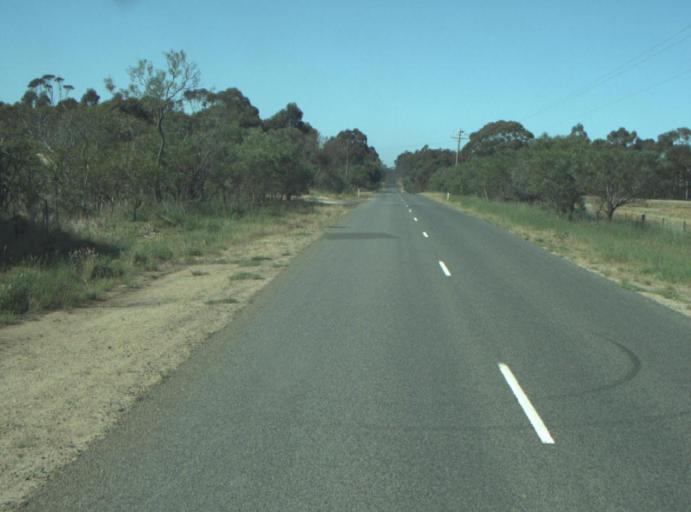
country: AU
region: Victoria
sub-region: Greater Geelong
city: Lara
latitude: -37.9355
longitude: 144.3937
